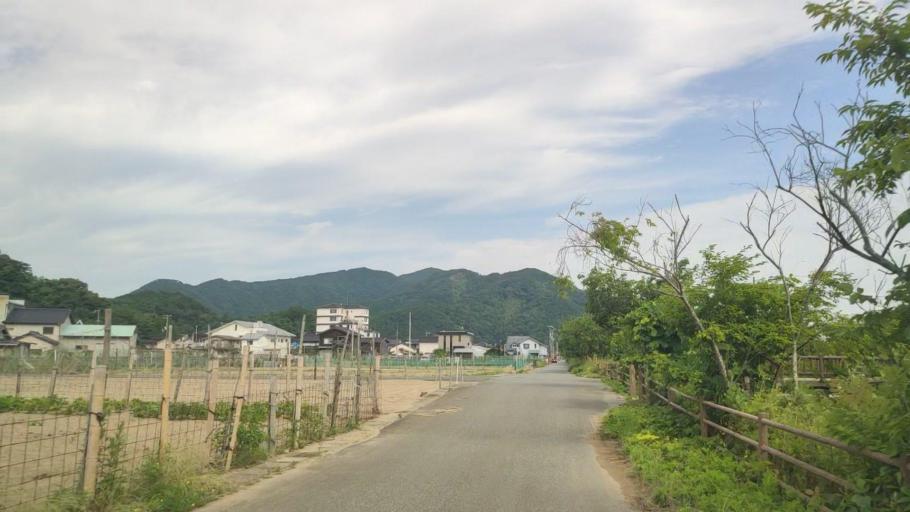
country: JP
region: Hyogo
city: Toyooka
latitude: 35.6403
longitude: 134.8386
